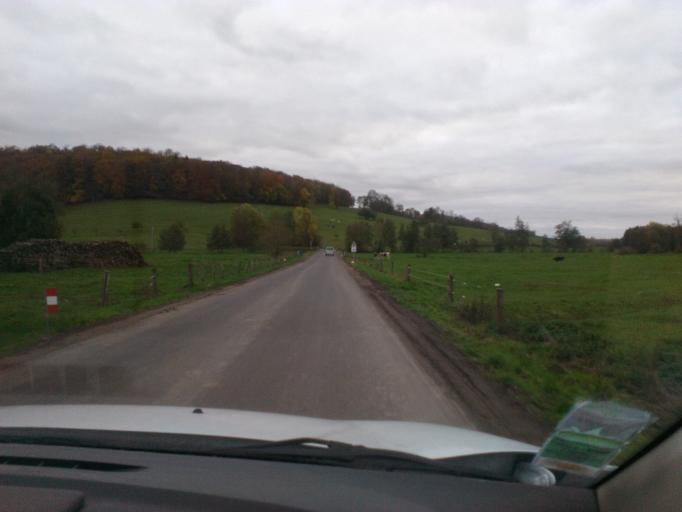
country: FR
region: Lorraine
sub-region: Departement des Vosges
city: Mirecourt
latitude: 48.2774
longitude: 6.2340
